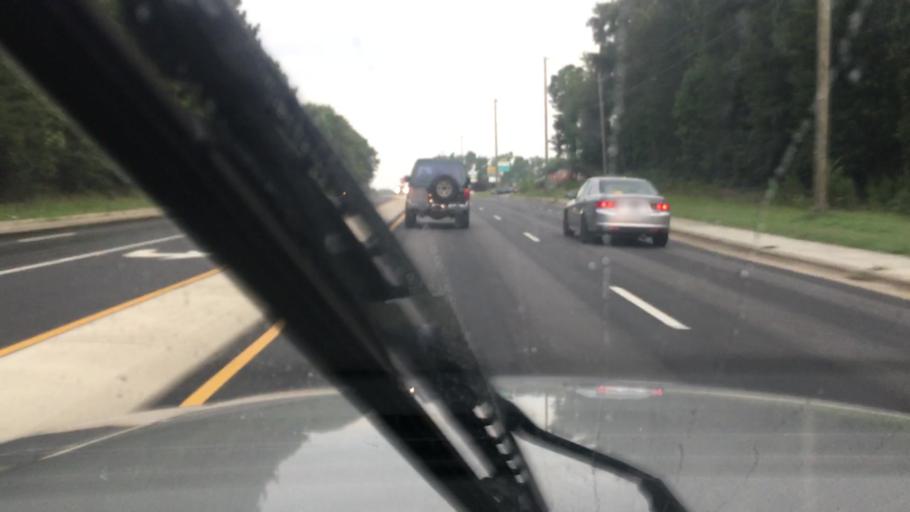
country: US
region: North Carolina
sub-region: Cumberland County
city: Fort Bragg
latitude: 35.0714
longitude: -79.0122
